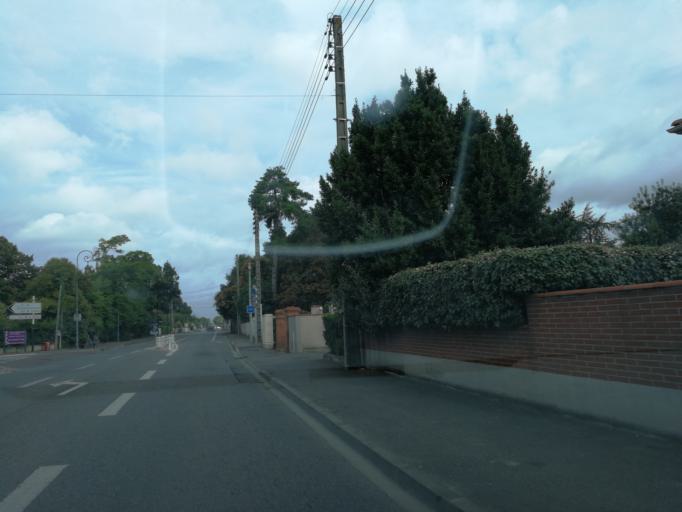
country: FR
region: Midi-Pyrenees
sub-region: Departement de la Haute-Garonne
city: Aucamville
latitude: 43.6705
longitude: 1.4277
